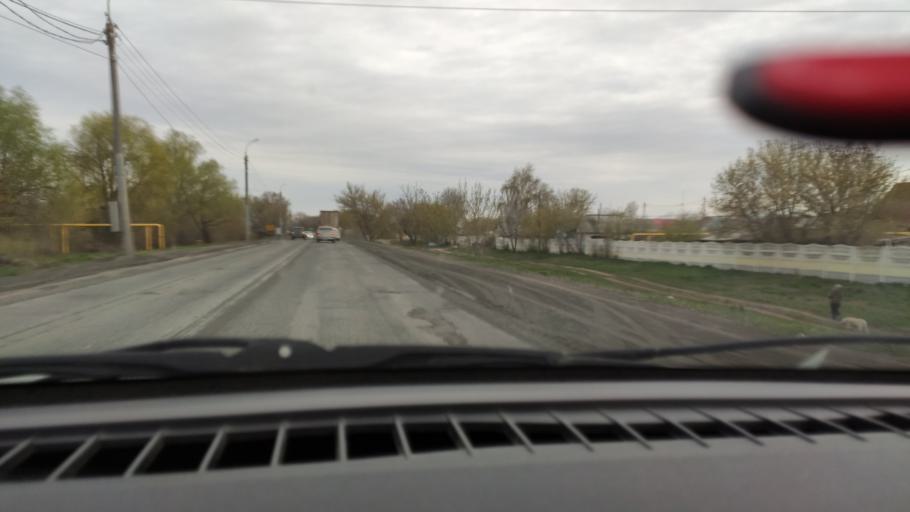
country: RU
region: Orenburg
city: Tatarskaya Kargala
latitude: 51.8623
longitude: 55.1363
